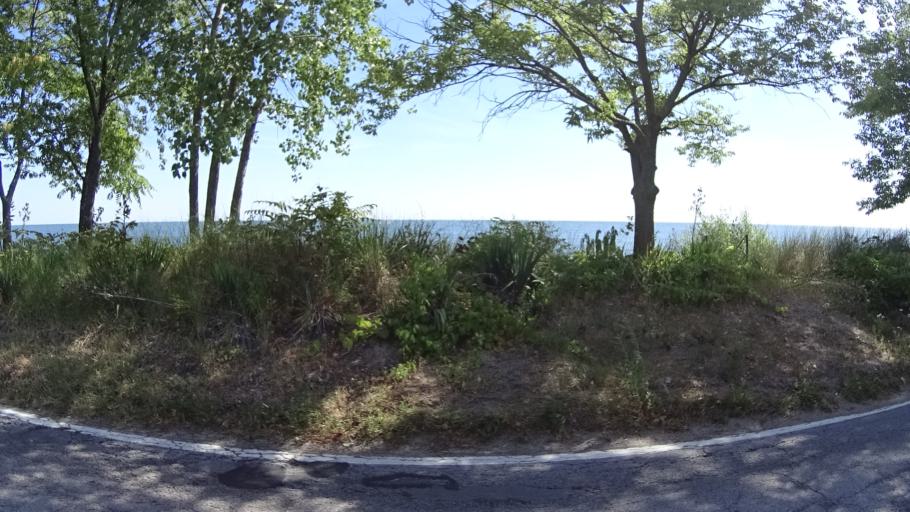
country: US
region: Ohio
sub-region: Erie County
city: Sandusky
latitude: 41.4621
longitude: -82.6597
